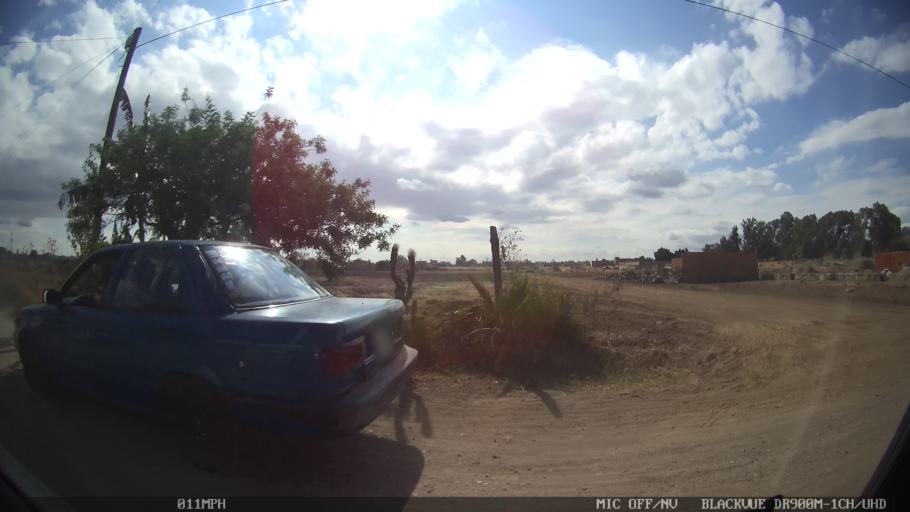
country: MX
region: Jalisco
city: Tonala
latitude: 20.6509
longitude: -103.2474
